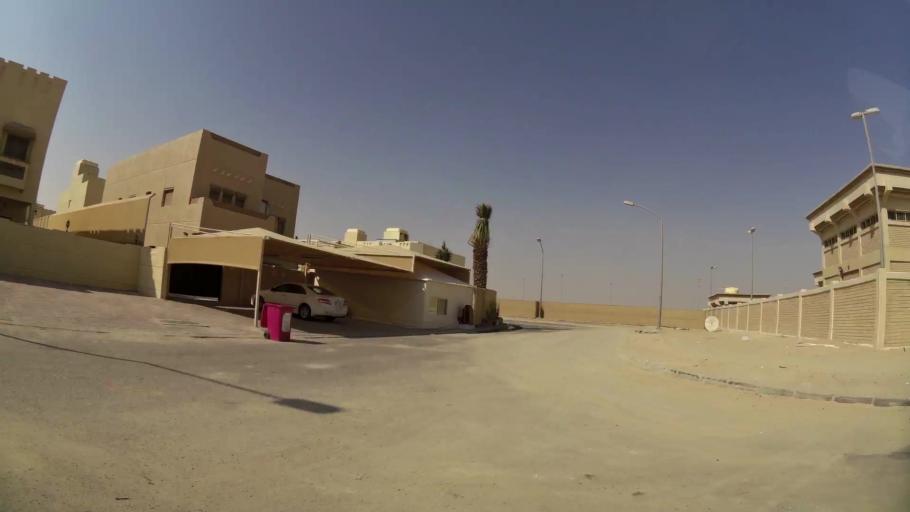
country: KW
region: Al Ahmadi
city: Al Wafrah
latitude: 28.8096
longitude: 48.0497
